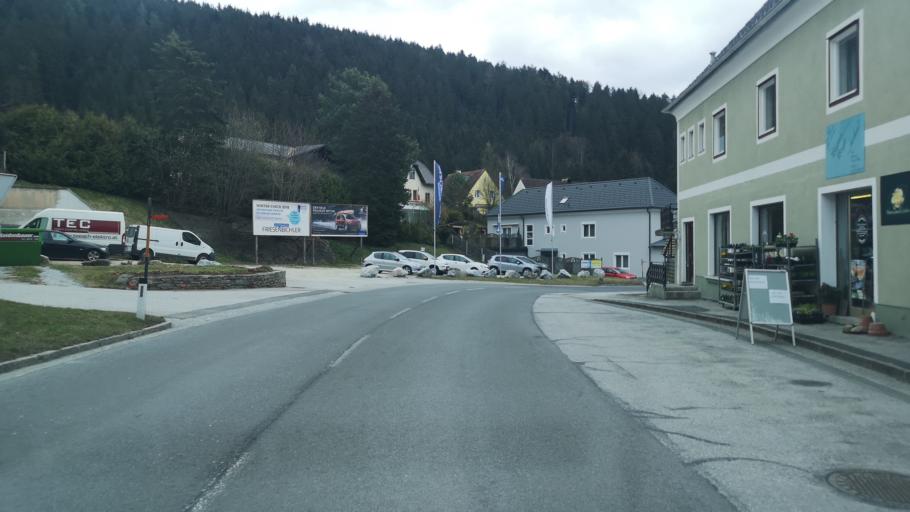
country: AT
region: Styria
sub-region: Politischer Bezirk Weiz
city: Birkfeld
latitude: 47.3570
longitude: 15.6986
